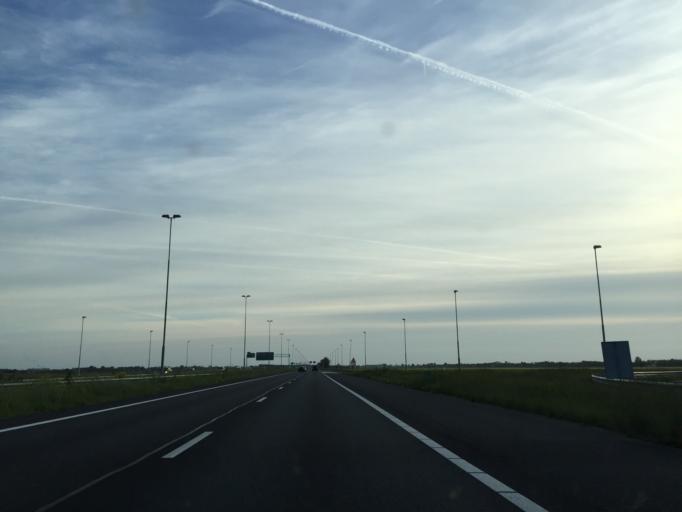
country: NL
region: North Holland
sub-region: Gemeente Beemster
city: Halfweg
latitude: 52.4948
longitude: 4.8977
